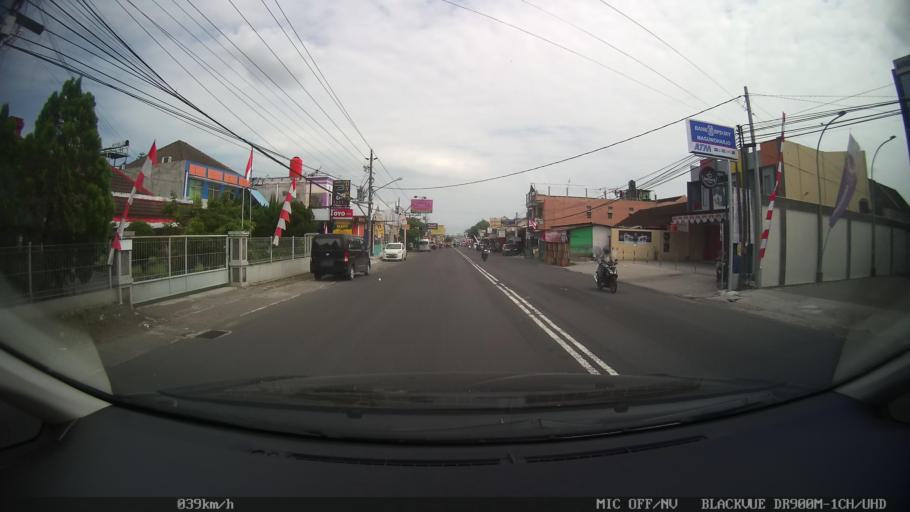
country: ID
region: Daerah Istimewa Yogyakarta
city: Depok
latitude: -7.7557
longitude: 110.4338
